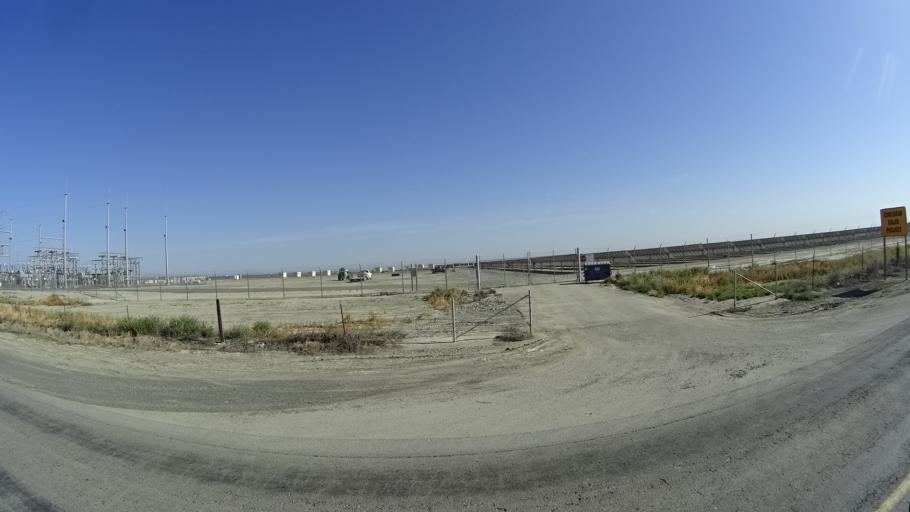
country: US
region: California
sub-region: Kings County
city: Corcoran
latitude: 36.1379
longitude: -119.5745
